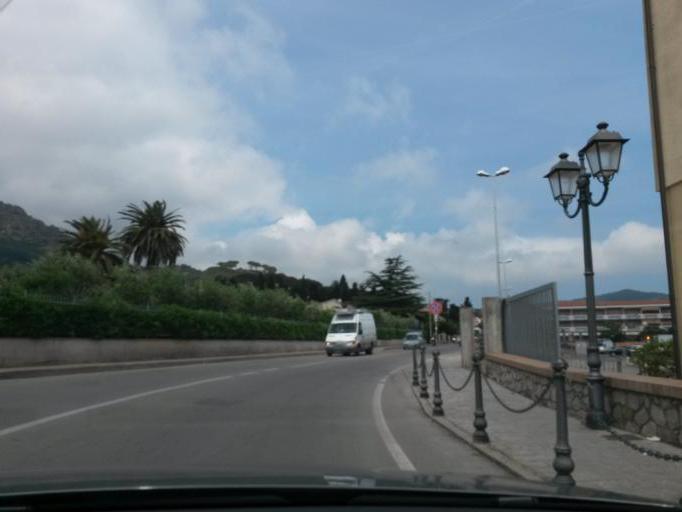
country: IT
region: Tuscany
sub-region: Provincia di Livorno
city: Porto Azzurro
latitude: 42.7675
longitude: 10.3946
